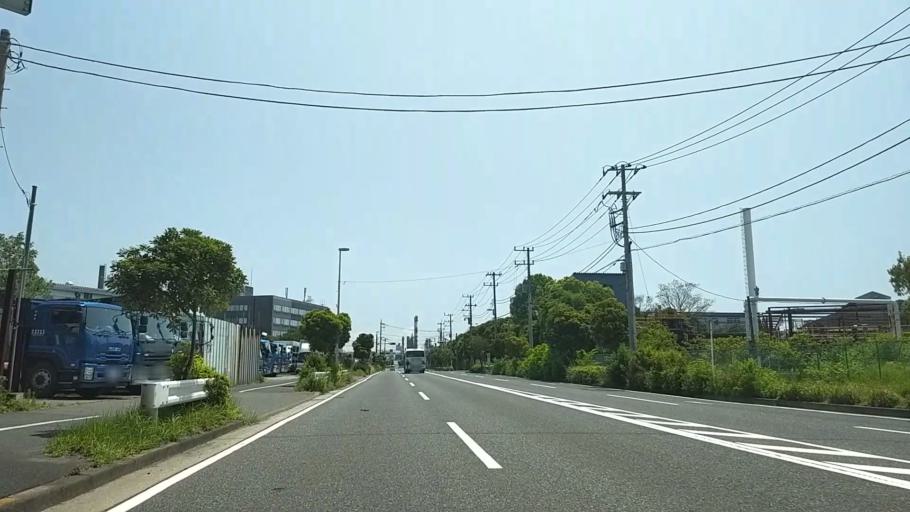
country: JP
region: Kanagawa
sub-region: Kawasaki-shi
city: Kawasaki
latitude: 35.5200
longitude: 139.7332
